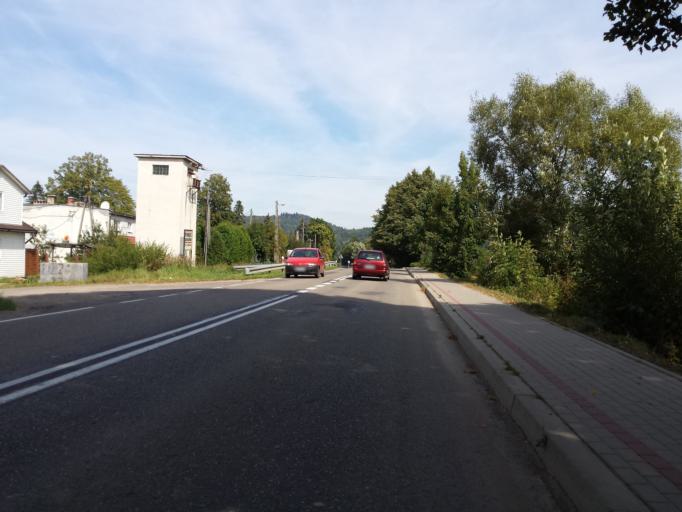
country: PL
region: Subcarpathian Voivodeship
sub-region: Powiat leski
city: Baligrod
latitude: 49.3431
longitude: 22.2900
